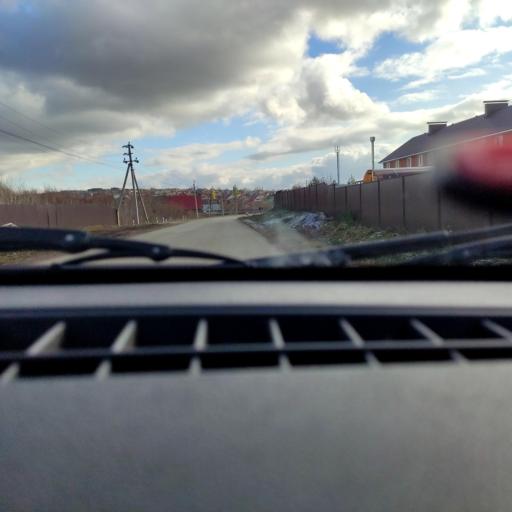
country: RU
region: Bashkortostan
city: Ufa
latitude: 54.5999
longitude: 55.9233
